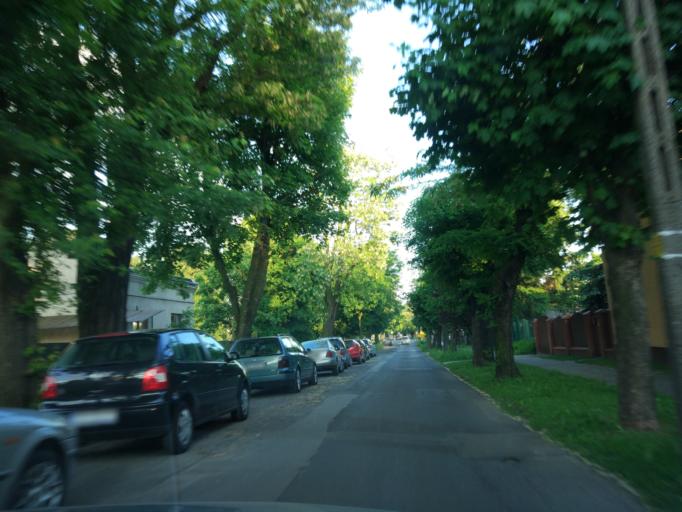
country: PL
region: Lodz Voivodeship
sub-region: Powiat kutnowski
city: Kutno
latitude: 52.2320
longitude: 19.3499
